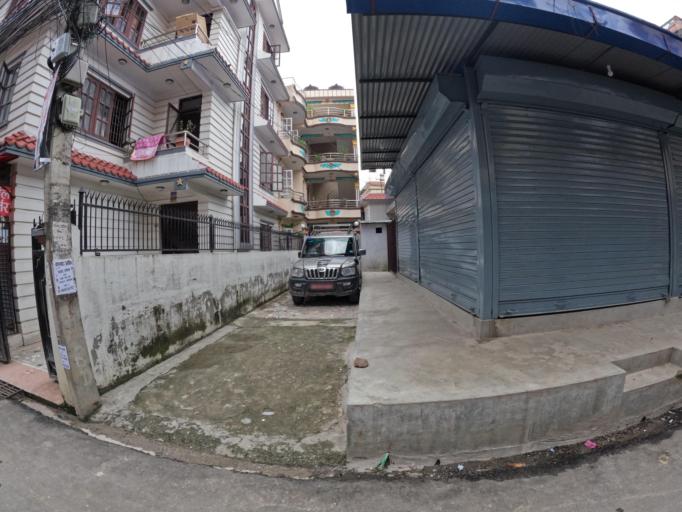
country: NP
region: Central Region
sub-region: Bagmati Zone
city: Kathmandu
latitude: 27.7454
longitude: 85.3172
